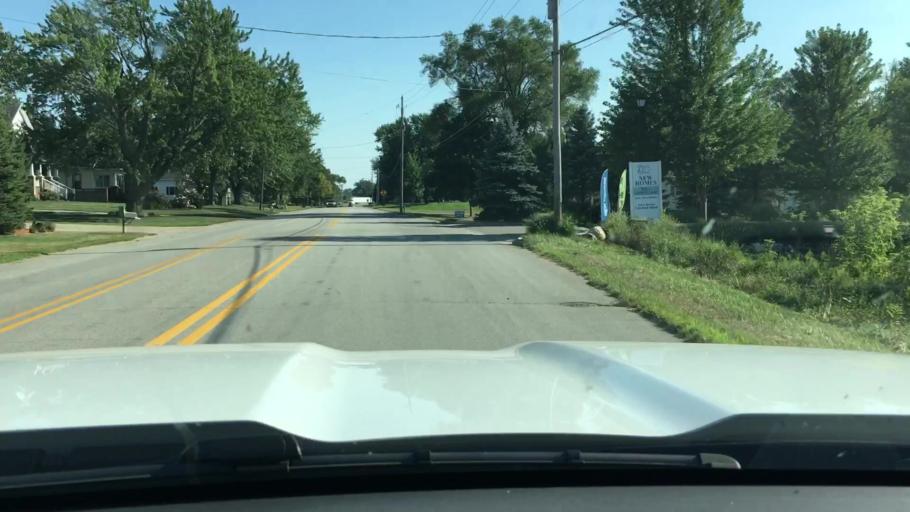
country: US
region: Michigan
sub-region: Ottawa County
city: Zeeland
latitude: 42.8159
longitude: -85.9401
